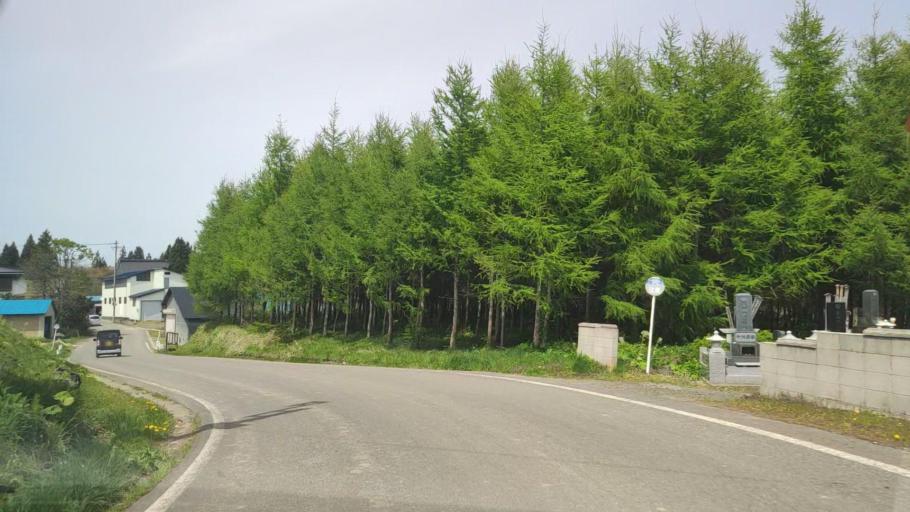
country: JP
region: Aomori
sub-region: Misawa Shi
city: Inuotose
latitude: 40.7786
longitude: 141.1228
